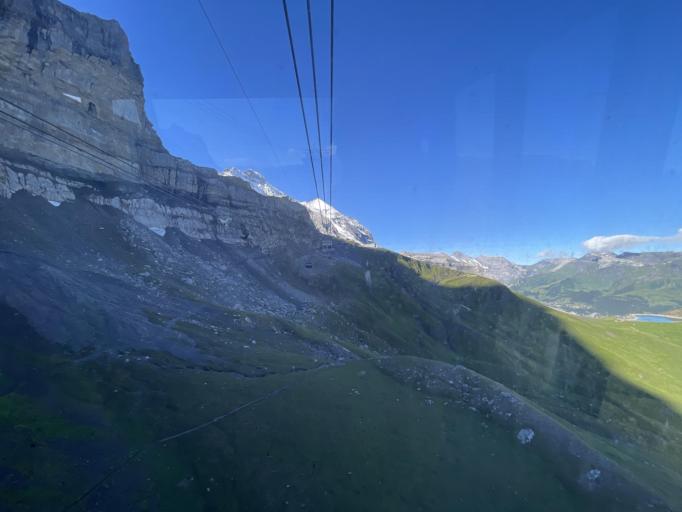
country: CH
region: Bern
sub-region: Interlaken-Oberhasli District
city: Grindelwald
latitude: 46.5804
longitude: 7.9801
